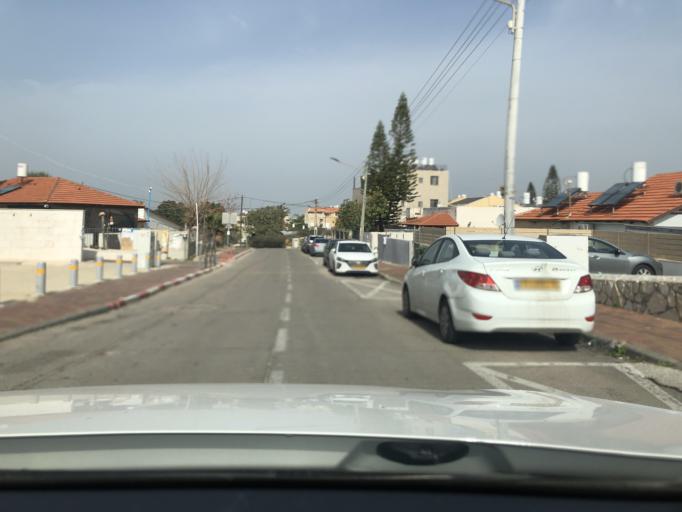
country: IL
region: Central District
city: Rosh Ha'Ayin
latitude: 32.0913
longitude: 34.9600
